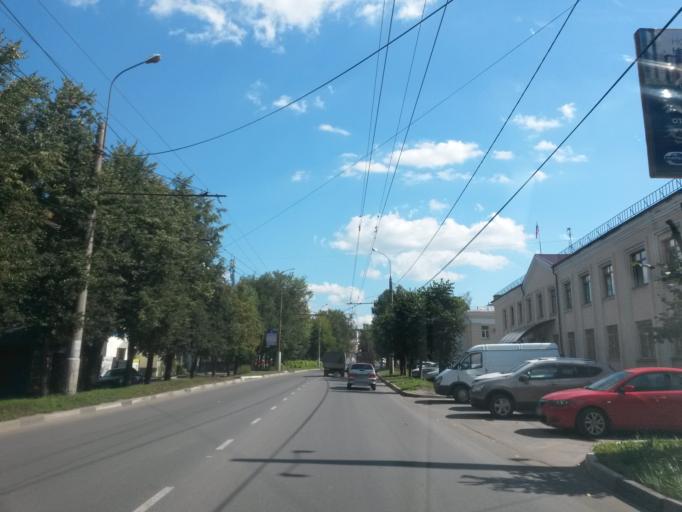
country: RU
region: Ivanovo
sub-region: Gorod Ivanovo
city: Ivanovo
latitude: 56.9866
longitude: 40.9889
